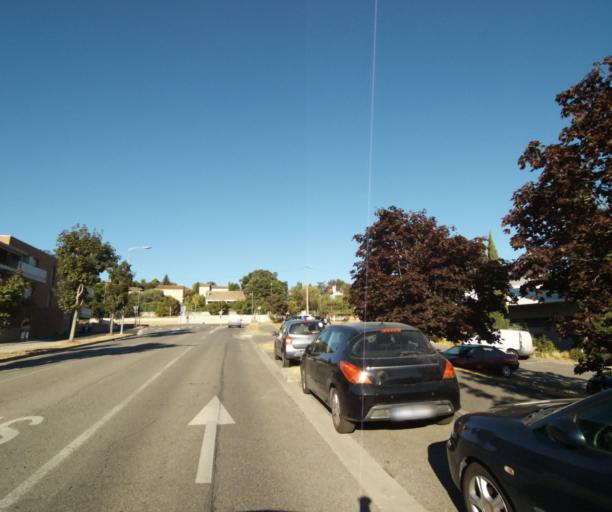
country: FR
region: Midi-Pyrenees
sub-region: Departement de la Haute-Garonne
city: Castanet-Tolosan
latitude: 43.5232
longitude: 1.4955
